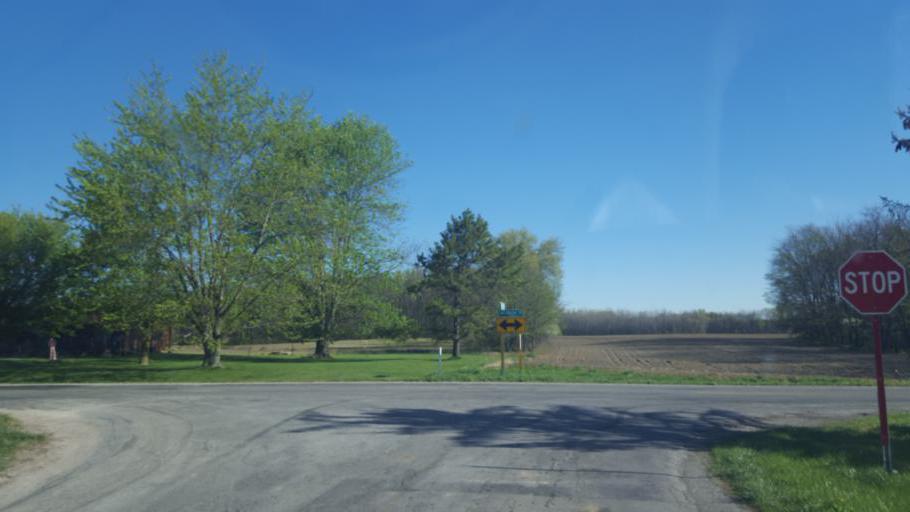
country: US
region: Ohio
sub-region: Crawford County
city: Bucyrus
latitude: 40.6522
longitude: -82.9649
